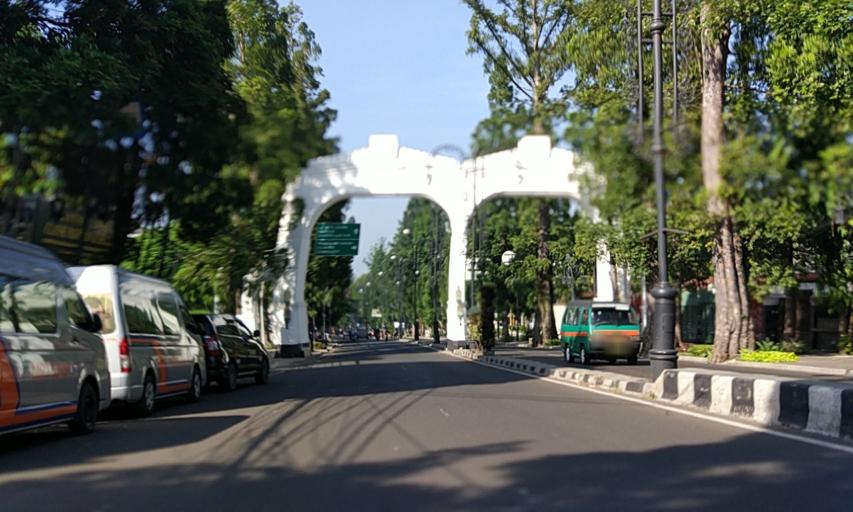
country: ID
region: West Java
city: Bandung
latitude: -6.8857
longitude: 107.6137
